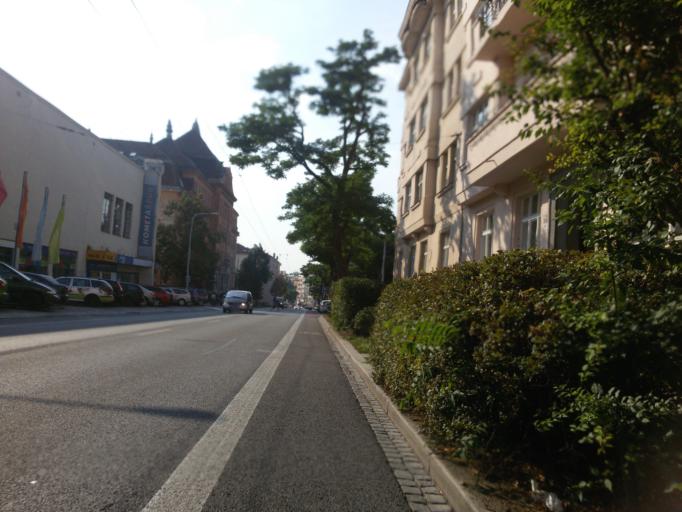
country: CZ
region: South Moravian
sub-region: Mesto Brno
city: Brno
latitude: 49.2033
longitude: 16.6000
